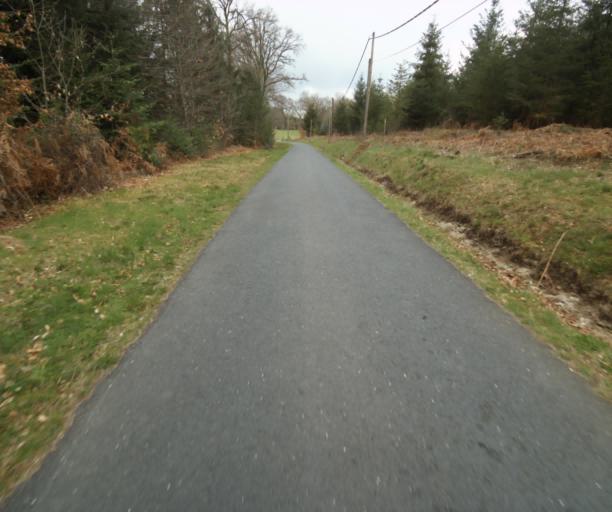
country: FR
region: Limousin
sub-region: Departement de la Correze
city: Correze
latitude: 45.3029
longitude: 1.9116
